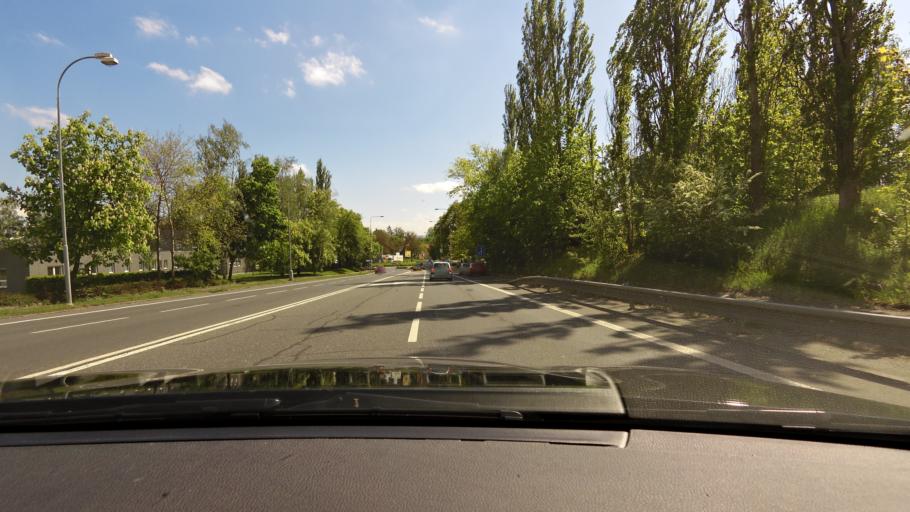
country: CZ
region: Plzensky
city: Klatovy
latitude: 49.4060
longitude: 13.2942
